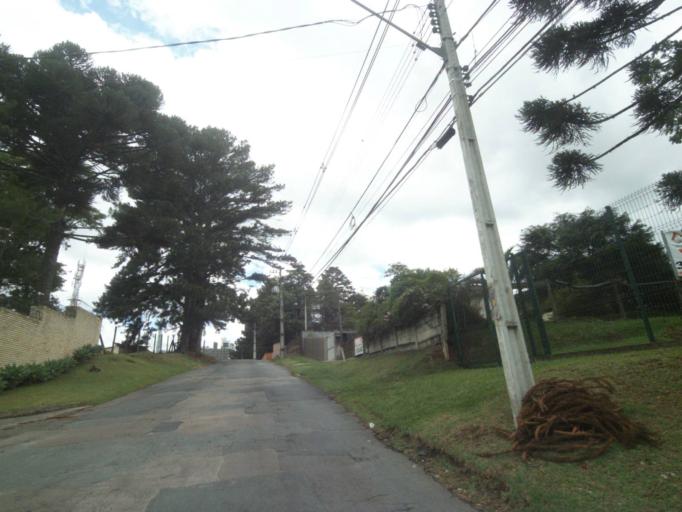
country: BR
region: Parana
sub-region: Curitiba
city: Curitiba
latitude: -25.4330
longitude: -49.3234
